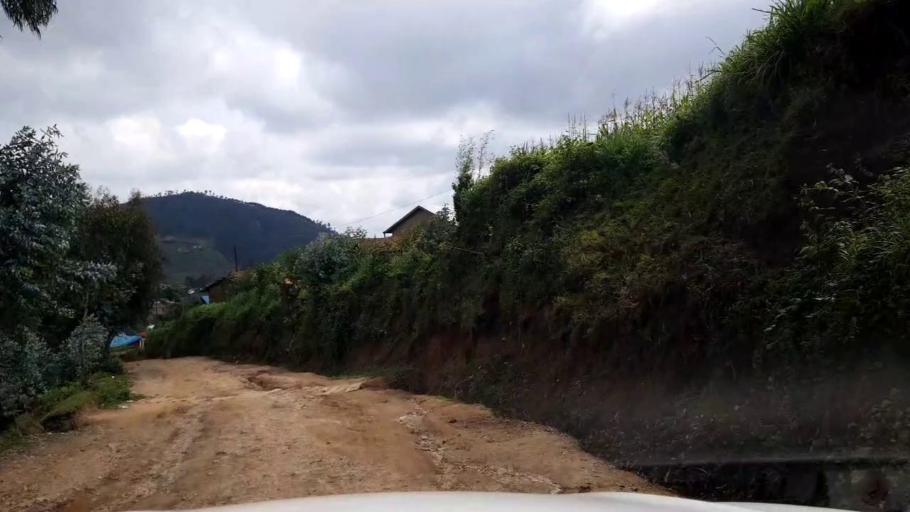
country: RW
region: Western Province
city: Kibuye
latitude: -1.9447
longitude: 29.4705
